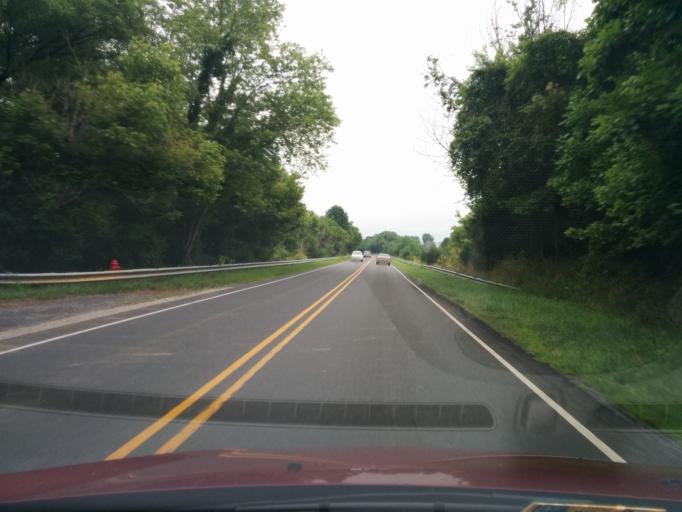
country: US
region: Virginia
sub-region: Rockbridge County
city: East Lexington
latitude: 37.8047
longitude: -79.4207
